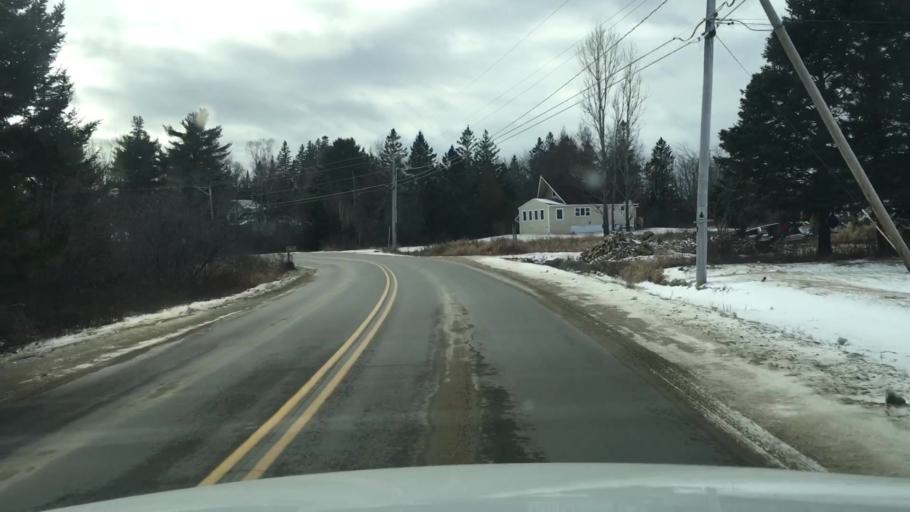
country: US
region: Maine
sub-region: Washington County
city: Jonesport
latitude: 44.6253
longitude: -67.6009
